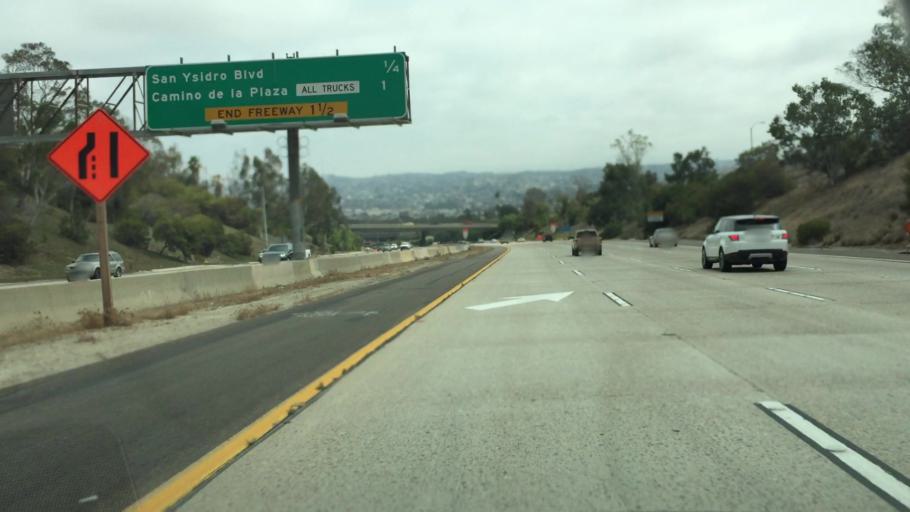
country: MX
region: Baja California
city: Tijuana
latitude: 32.5621
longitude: -117.0421
